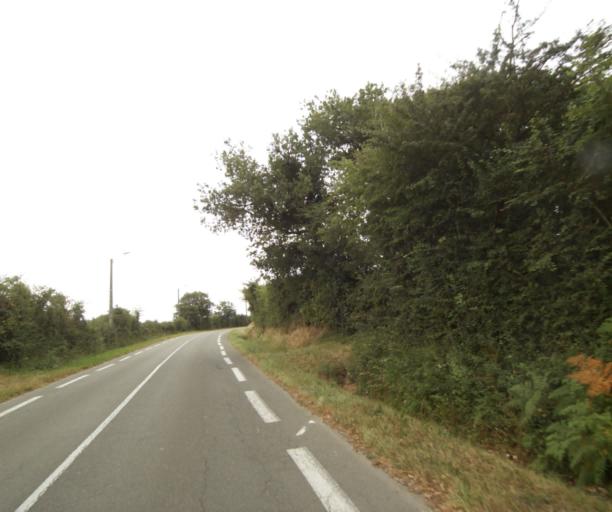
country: FR
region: Pays de la Loire
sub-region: Departement de la Vendee
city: Chateau-d'Olonne
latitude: 46.4977
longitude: -1.7334
